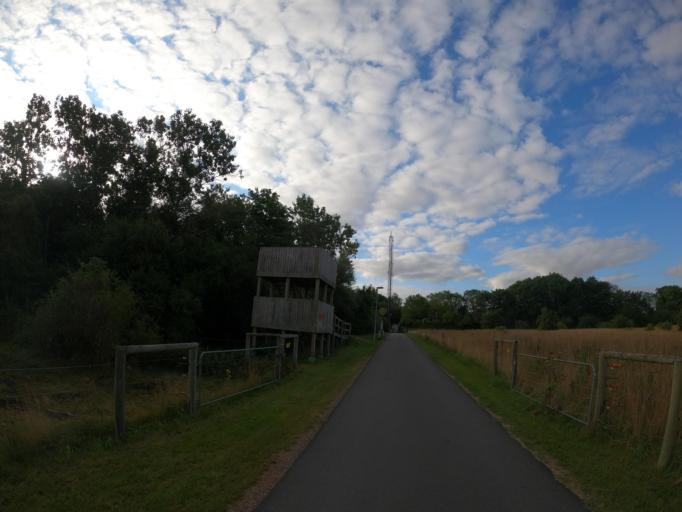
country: SE
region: Skane
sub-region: Staffanstorps Kommun
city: Staffanstorp
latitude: 55.6565
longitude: 13.2129
